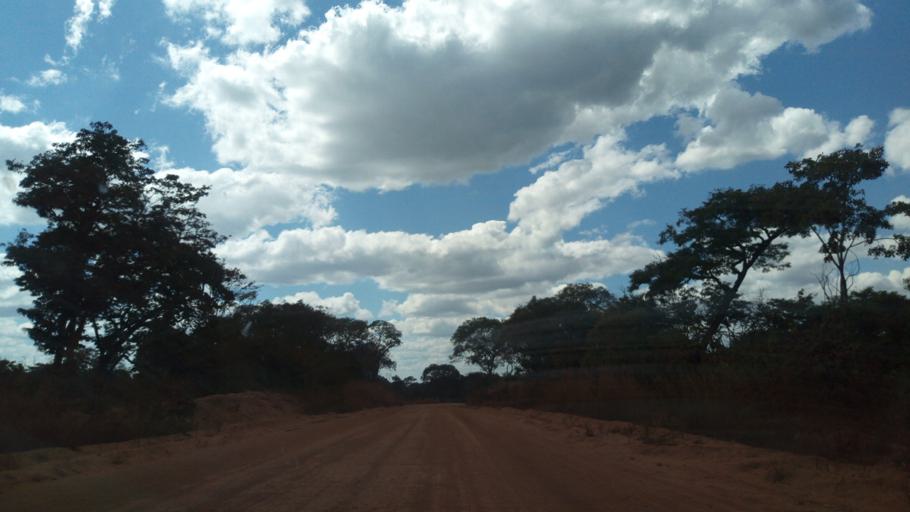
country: ZM
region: Copperbelt
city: Mufulira
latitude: -12.0325
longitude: 28.6717
